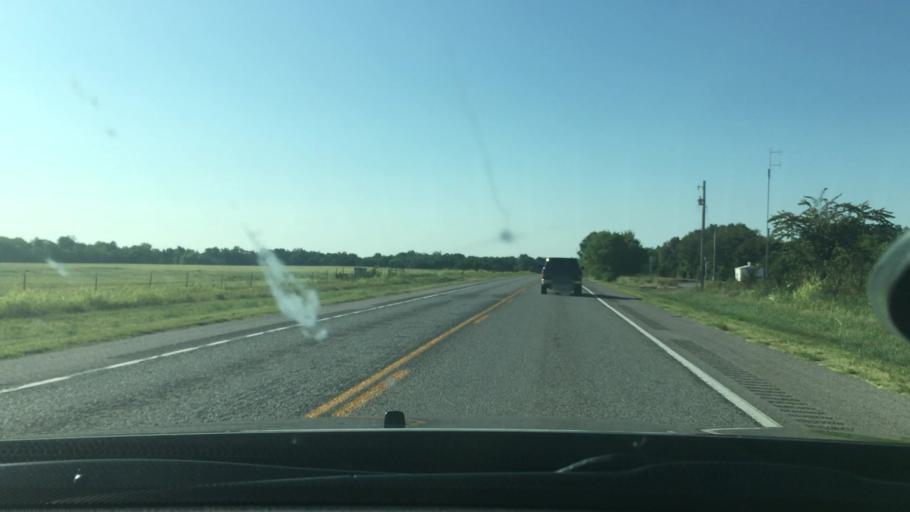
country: US
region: Oklahoma
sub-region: Johnston County
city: Tishomingo
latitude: 34.2575
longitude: -96.7663
